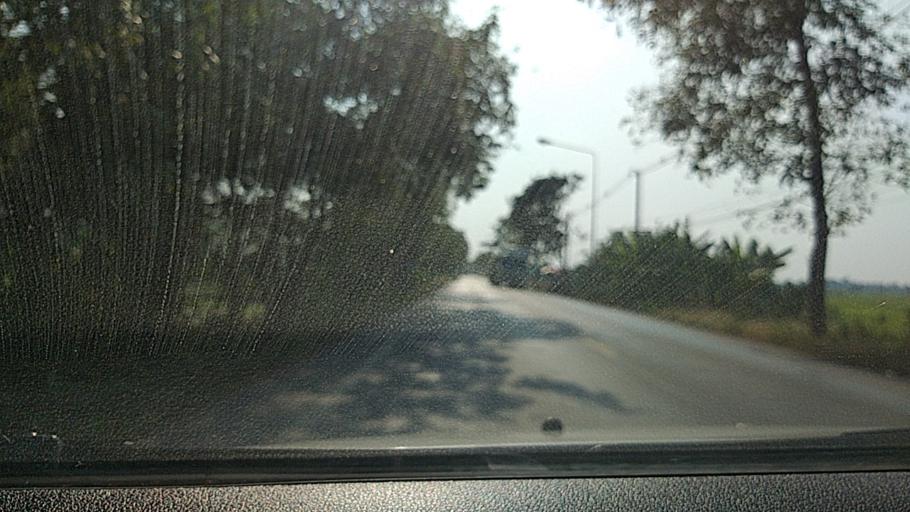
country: TH
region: Ang Thong
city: Chaiyo
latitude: 14.7229
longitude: 100.4523
